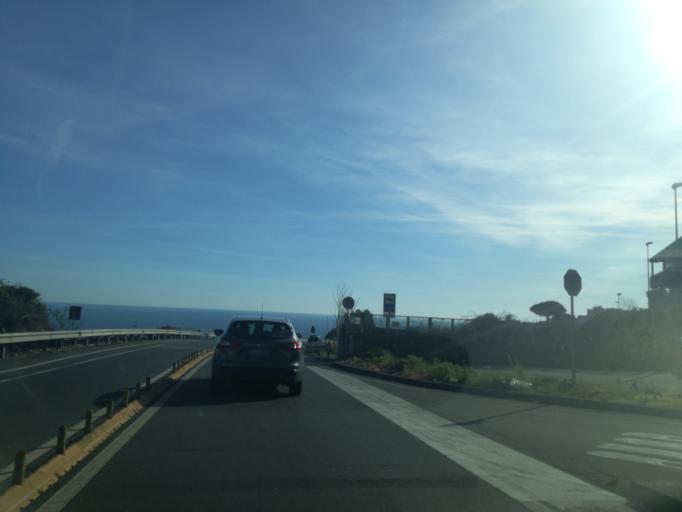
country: IT
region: Sicily
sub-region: Catania
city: Acireale
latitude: 37.6171
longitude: 15.1700
